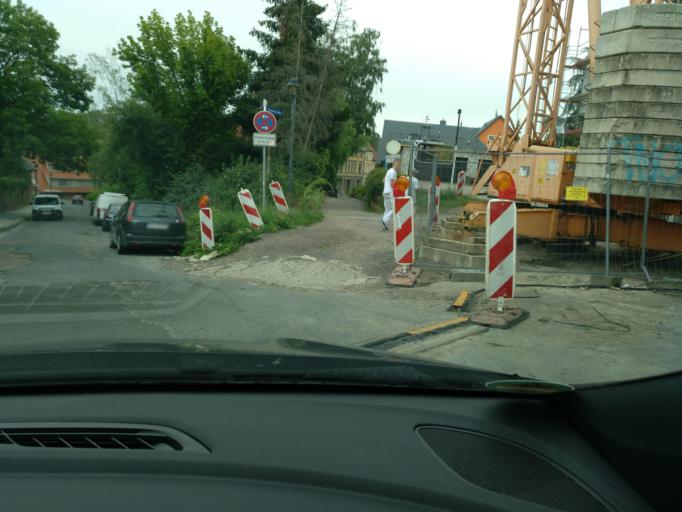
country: DE
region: Saxony-Anhalt
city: Sennewitz
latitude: 51.5077
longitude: 11.9511
